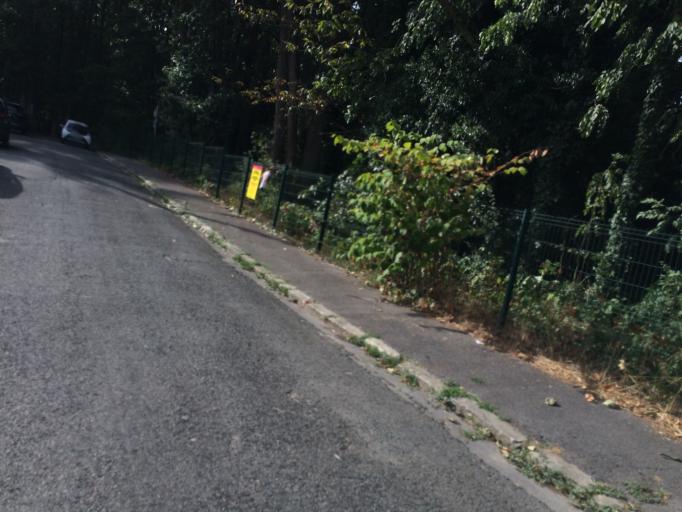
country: FR
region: Ile-de-France
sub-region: Departement de l'Essonne
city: Orsay
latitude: 48.7104
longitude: 2.1938
